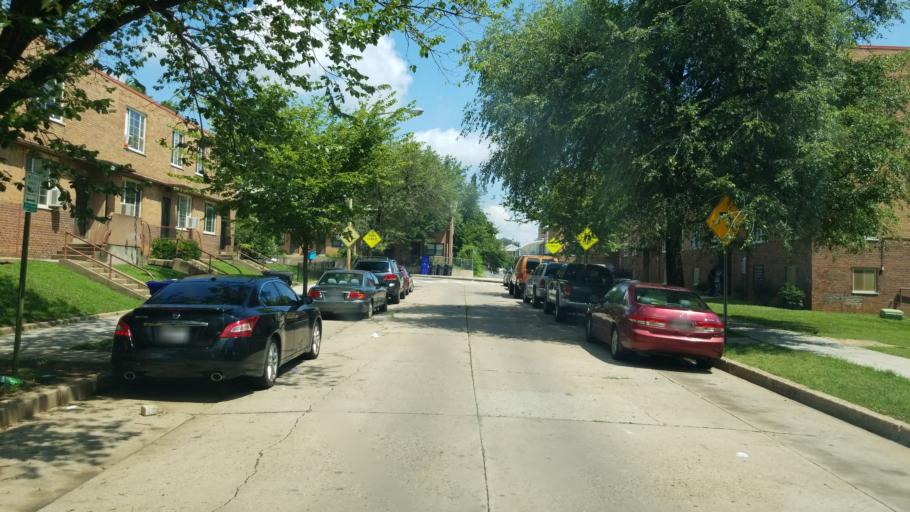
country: US
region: Maryland
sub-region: Prince George's County
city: Mount Rainier
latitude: 38.8997
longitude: -76.9723
